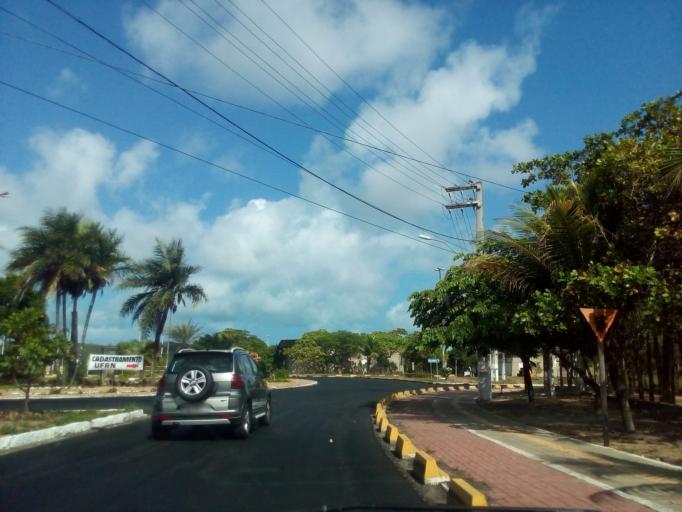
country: BR
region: Rio Grande do Norte
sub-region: Natal
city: Natal
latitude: -5.8379
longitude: -35.2059
